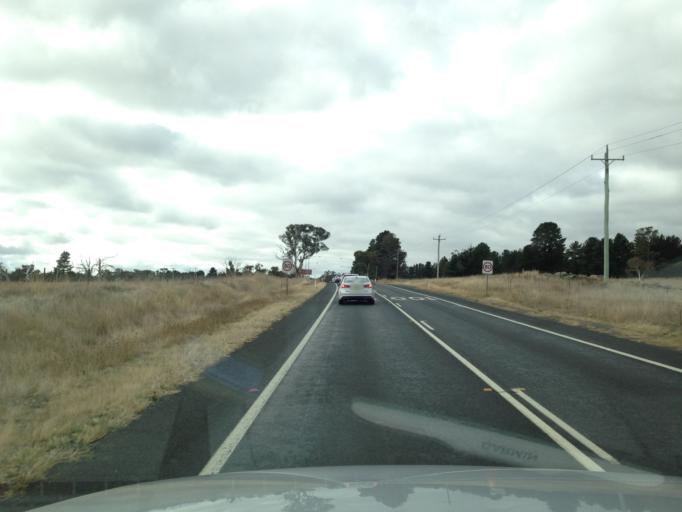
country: AU
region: New South Wales
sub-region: Cooma-Monaro
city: Cooma
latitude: -36.2484
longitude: 149.0482
